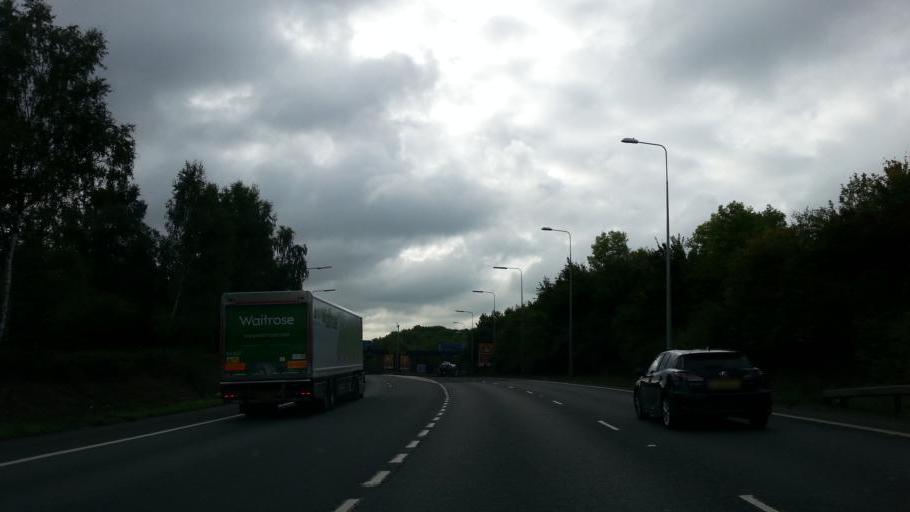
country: GB
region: England
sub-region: Hertfordshire
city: Abbots Langley
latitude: 51.7200
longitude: -0.3858
